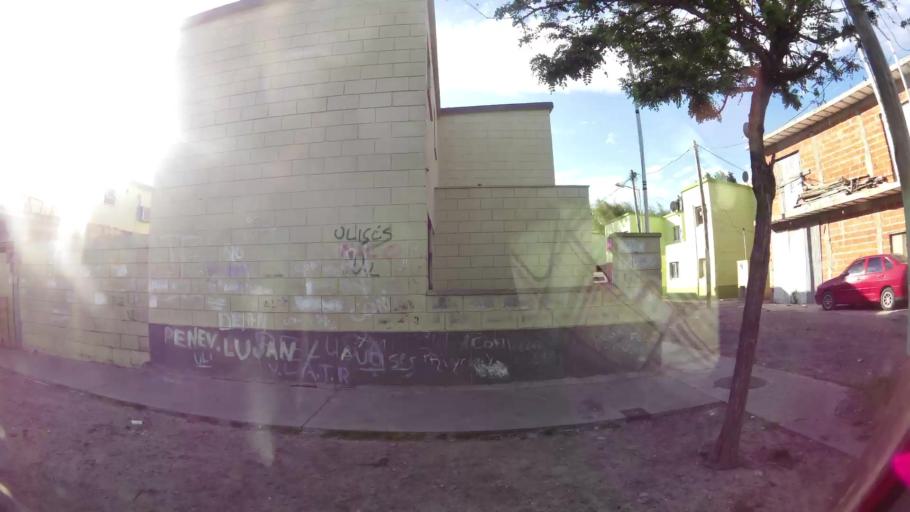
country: AR
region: Buenos Aires
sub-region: Partido de Avellaneda
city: Avellaneda
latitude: -34.6951
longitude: -58.3539
